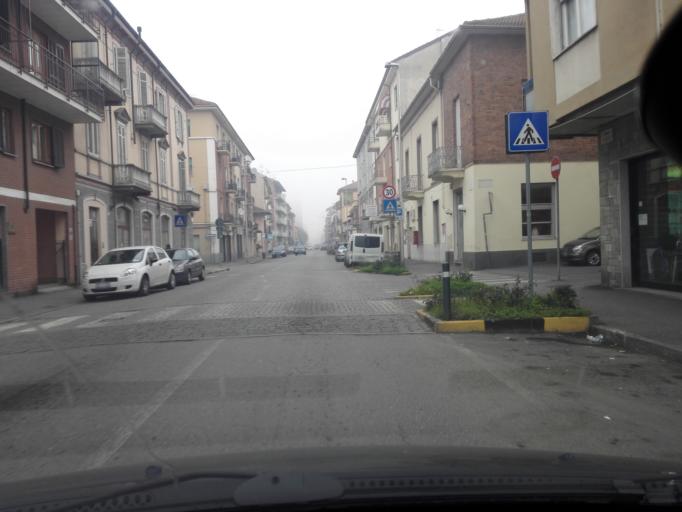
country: IT
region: Piedmont
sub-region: Provincia di Alessandria
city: Alessandria
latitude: 44.8986
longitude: 8.5983
